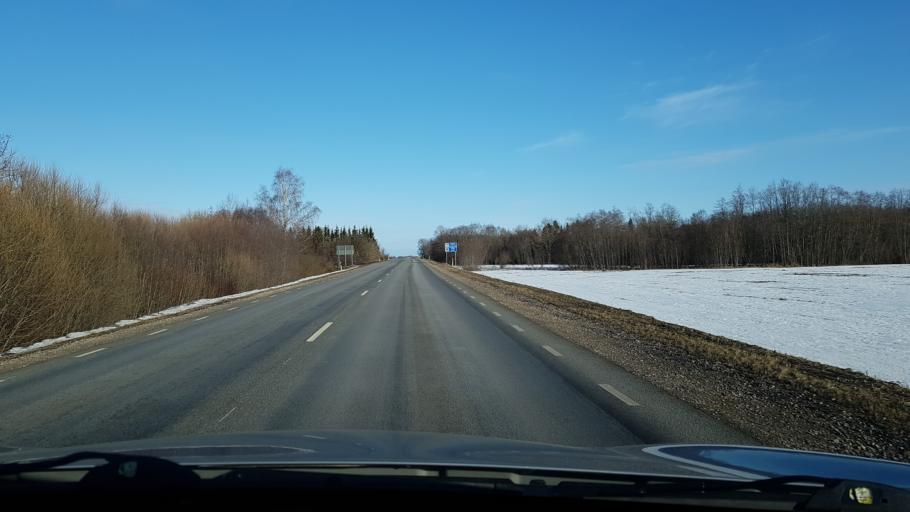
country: EE
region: Viljandimaa
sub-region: Vohma linn
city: Vohma
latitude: 58.6350
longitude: 25.5736
